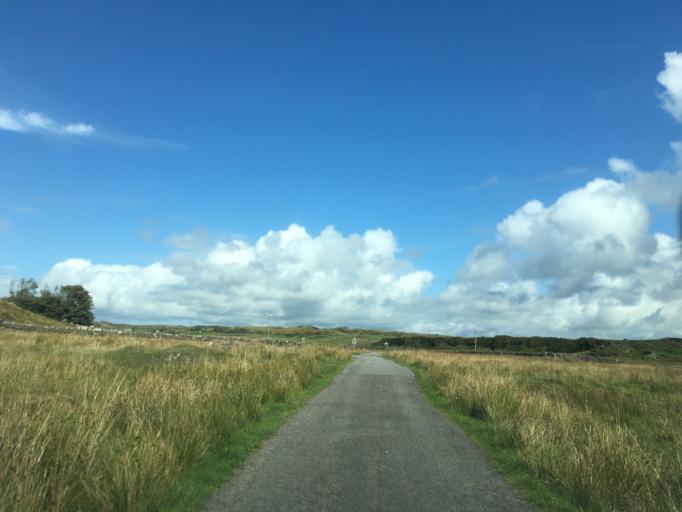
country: GB
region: Scotland
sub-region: Argyll and Bute
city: Isle Of Mull
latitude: 56.2173
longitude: -5.6538
